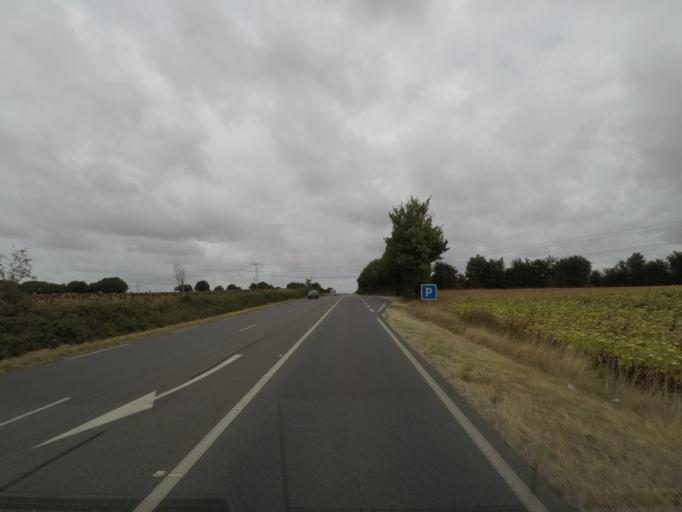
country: FR
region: Poitou-Charentes
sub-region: Departement des Deux-Sevres
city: Thorigne
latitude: 46.2743
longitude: -0.2394
